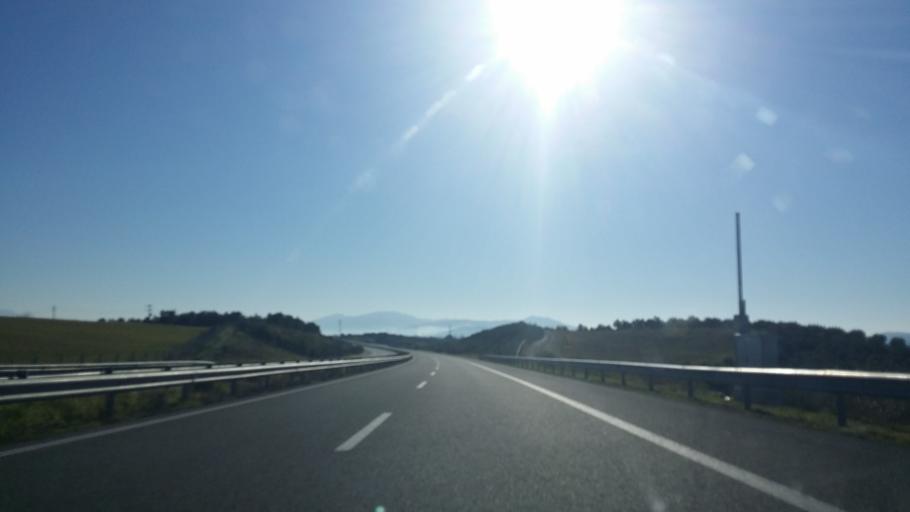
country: GR
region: West Greece
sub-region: Nomos Aitolias kai Akarnanias
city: Fitiai
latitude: 38.6782
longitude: 21.2207
